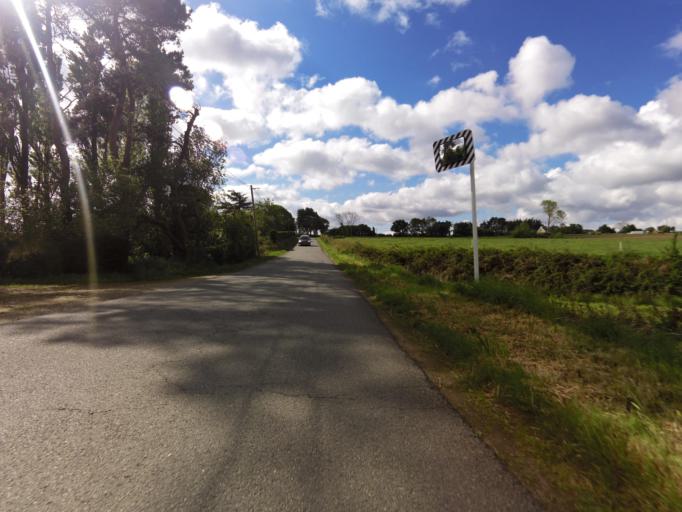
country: FR
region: Brittany
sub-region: Departement du Morbihan
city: Baden
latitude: 47.6295
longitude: -2.8969
